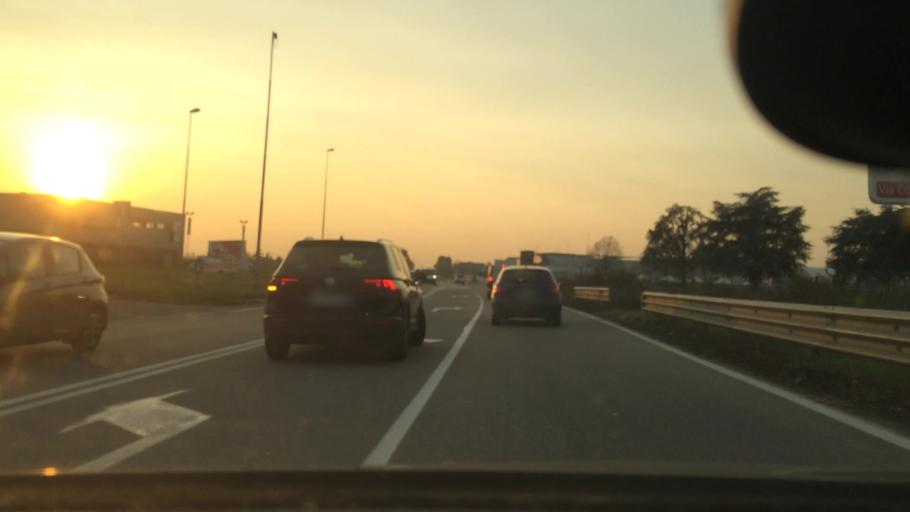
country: IT
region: Lombardy
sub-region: Provincia di Varese
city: Caronno Pertusella
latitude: 45.6173
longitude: 9.0550
